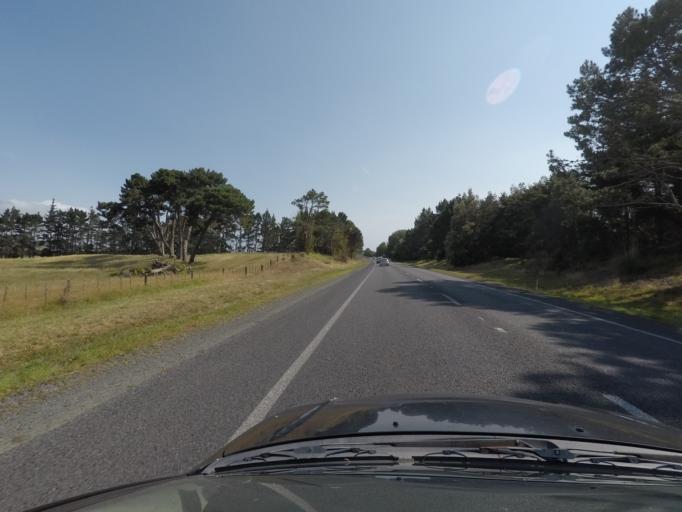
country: NZ
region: Northland
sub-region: Whangarei
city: Ruakaka
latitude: -35.9579
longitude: 174.4504
